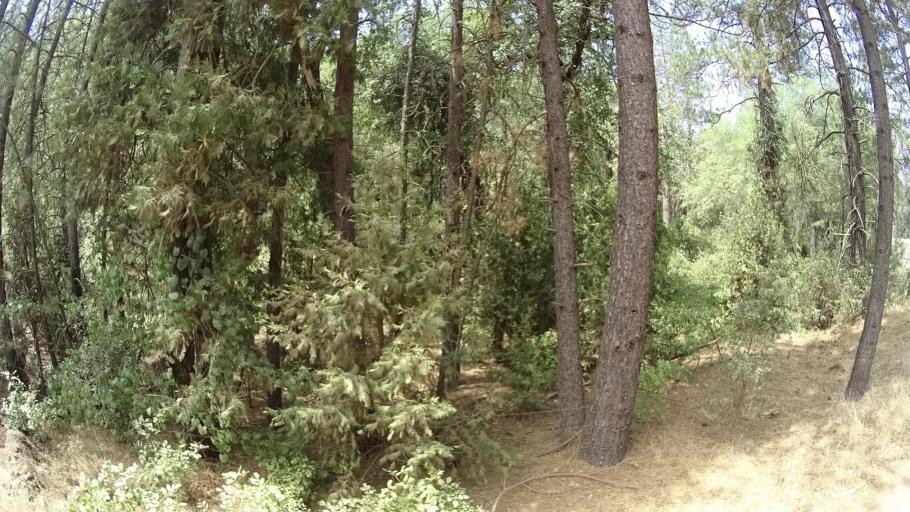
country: US
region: California
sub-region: Mariposa County
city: Midpines
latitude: 37.7446
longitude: -120.0331
